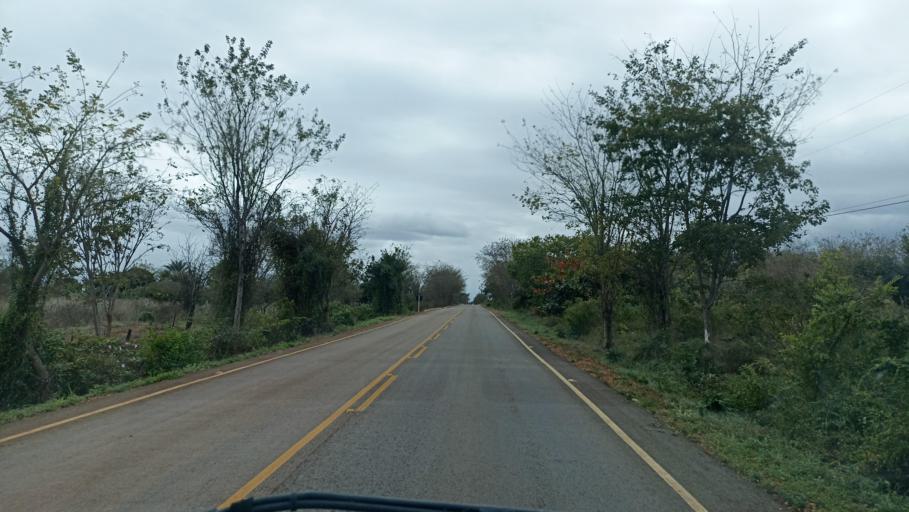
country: BR
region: Bahia
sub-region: Andarai
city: Vera Cruz
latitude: -12.9788
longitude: -41.0173
